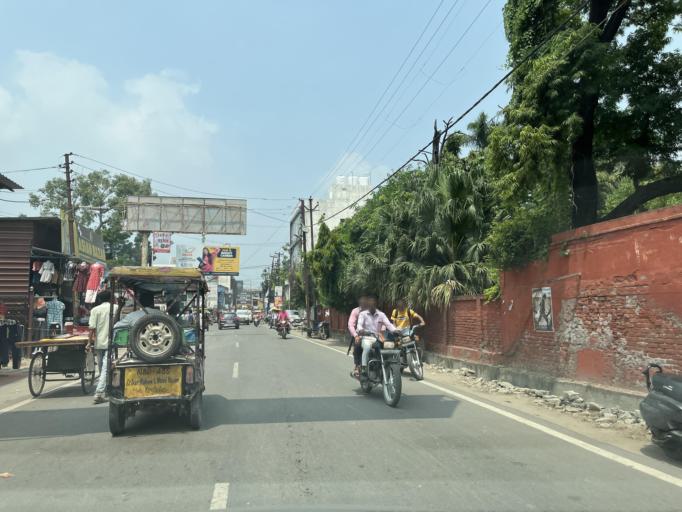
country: IN
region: Uttar Pradesh
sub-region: Bijnor
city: Najibabad
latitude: 29.6062
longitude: 78.3385
